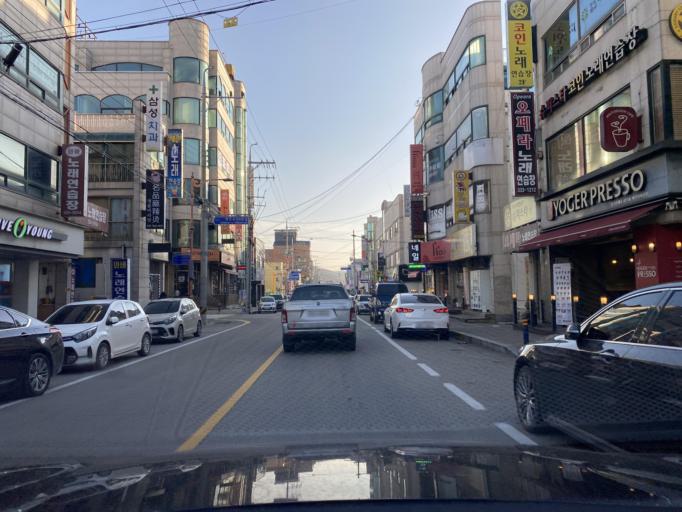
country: KR
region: Chungcheongnam-do
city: Yesan
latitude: 36.6915
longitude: 126.8301
